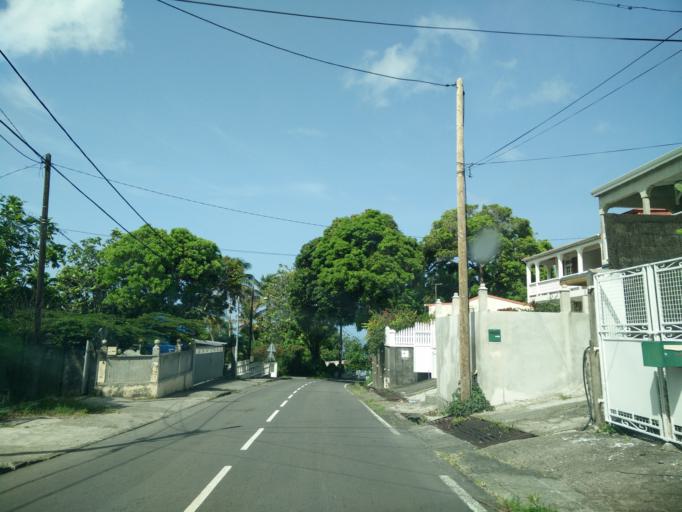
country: GP
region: Guadeloupe
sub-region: Guadeloupe
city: Basse-Terre
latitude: 15.9908
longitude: -61.7102
